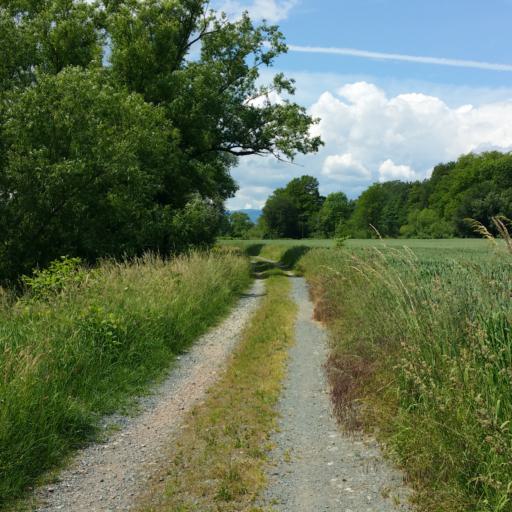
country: AT
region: Styria
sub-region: Politischer Bezirk Leibnitz
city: Gleinstatten
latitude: 46.7485
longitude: 15.3618
